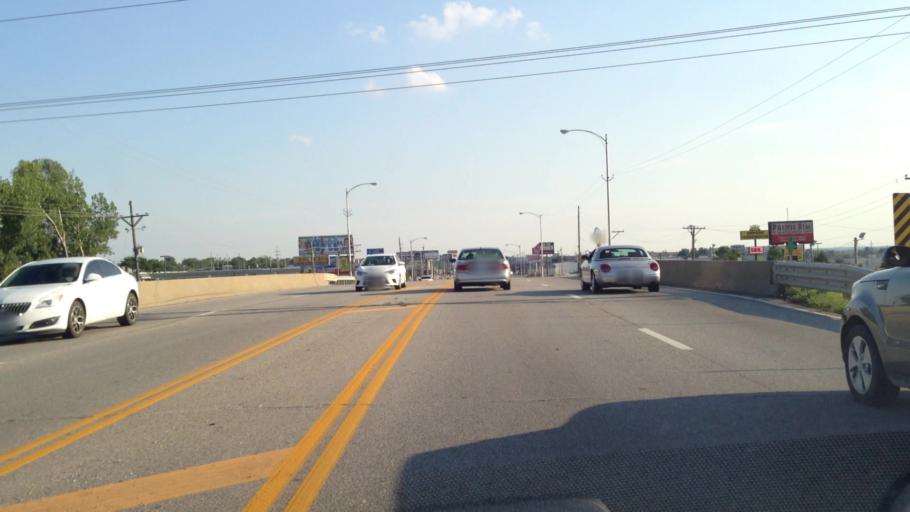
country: US
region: Missouri
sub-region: Jasper County
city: Duquesne
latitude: 37.0585
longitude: -94.4775
